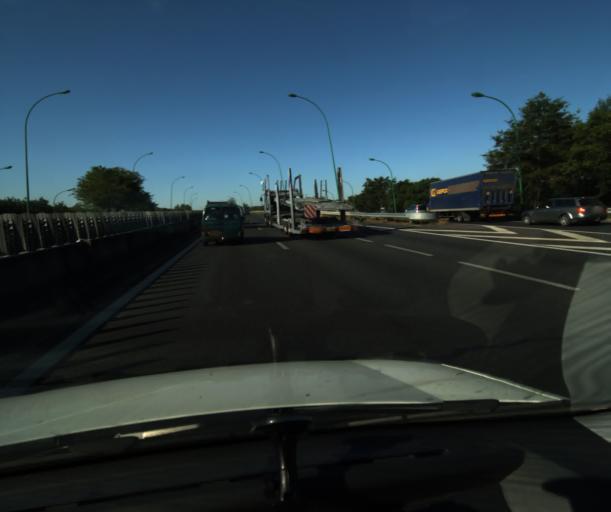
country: FR
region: Midi-Pyrenees
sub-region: Departement de la Haute-Garonne
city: Ramonville-Saint-Agne
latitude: 43.5747
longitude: 1.4962
